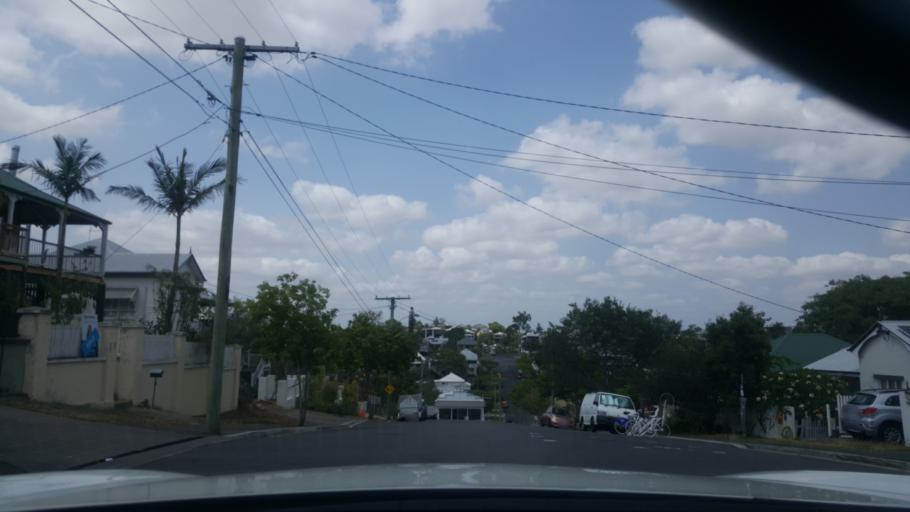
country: AU
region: Queensland
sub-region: Brisbane
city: South Brisbane
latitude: -27.4872
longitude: 153.0225
